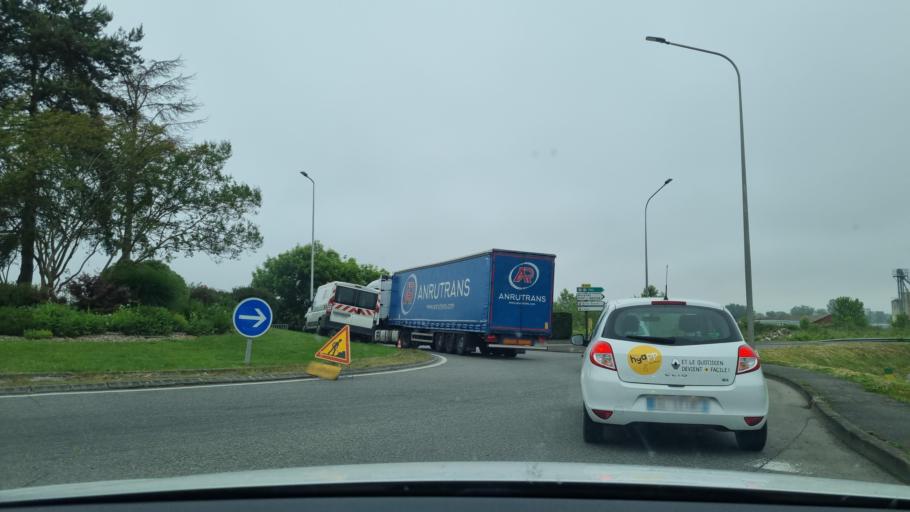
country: FR
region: Aquitaine
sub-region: Departement des Pyrenees-Atlantiques
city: Orthez
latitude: 43.4773
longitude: -0.7619
